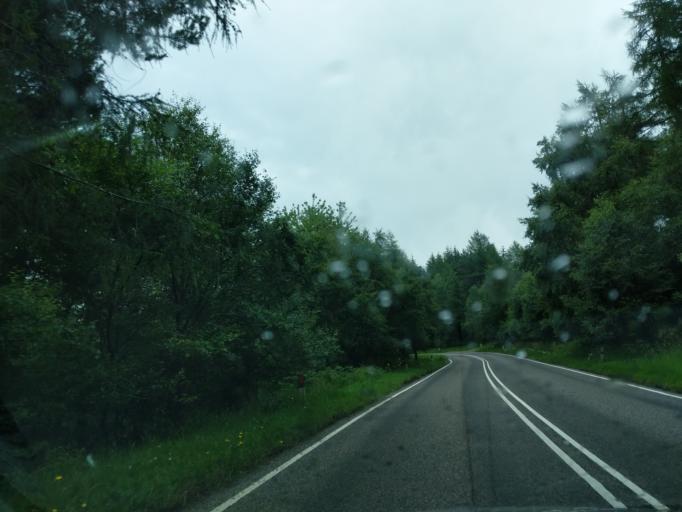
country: GB
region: Scotland
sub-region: Moray
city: Dufftown
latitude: 57.4779
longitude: -3.1641
